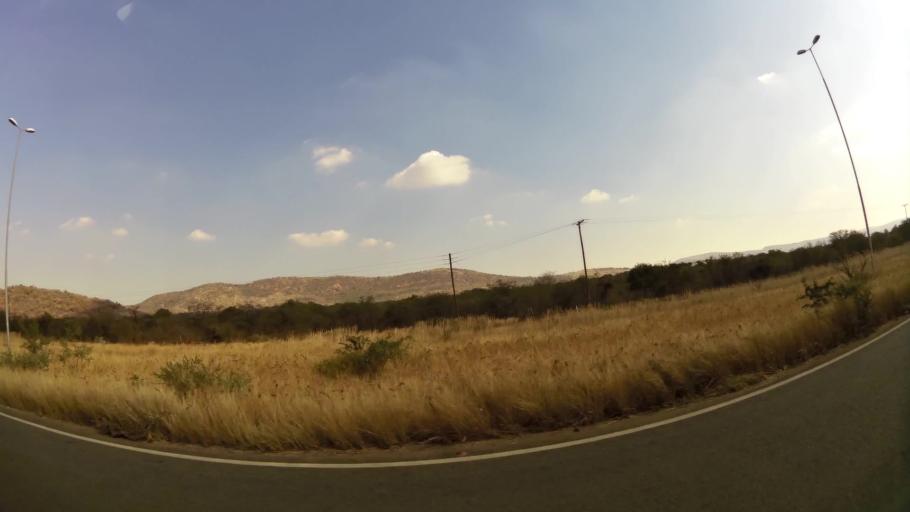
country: ZA
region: North-West
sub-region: Bojanala Platinum District Municipality
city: Rustenburg
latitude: -25.5347
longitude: 27.1188
